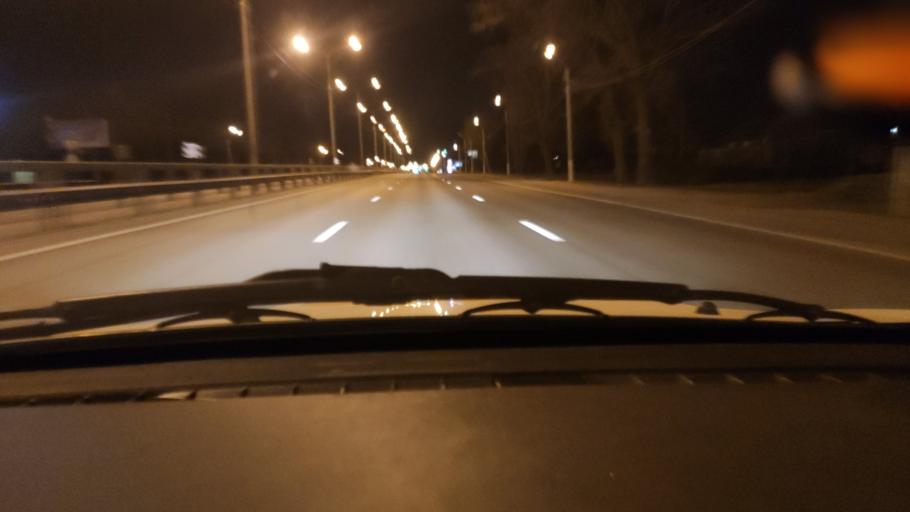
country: RU
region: Voronezj
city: Novaya Usman'
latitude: 51.6285
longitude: 39.3463
